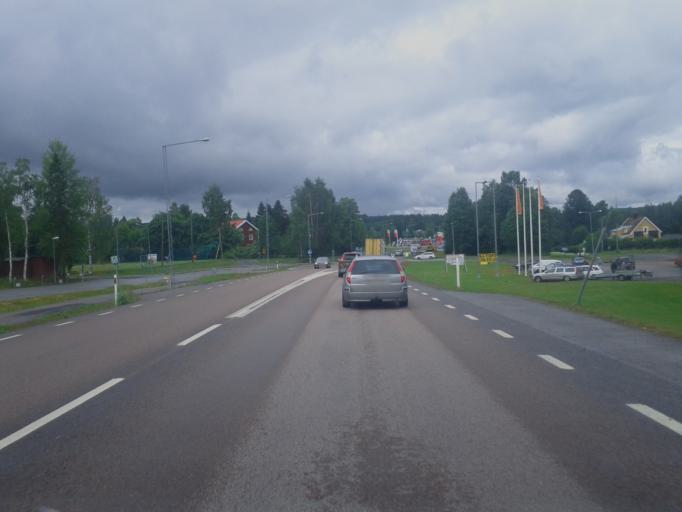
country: SE
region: Vaesternorrland
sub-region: Haernoesands Kommun
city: Haernoesand
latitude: 62.6705
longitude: 17.8403
